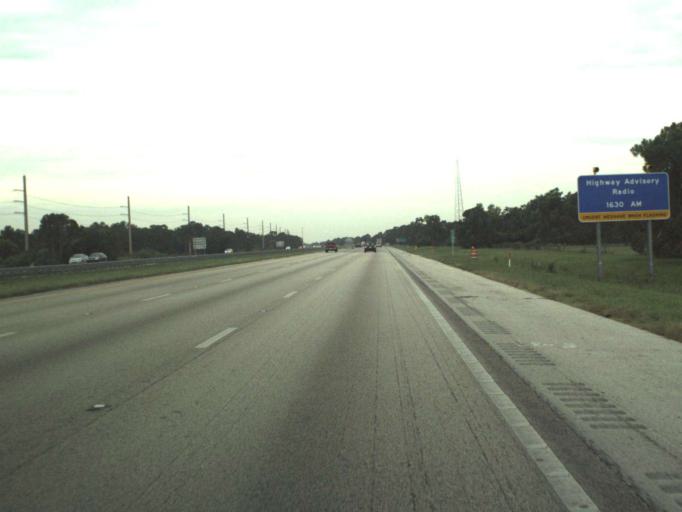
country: US
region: Florida
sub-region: Martin County
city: Palm City
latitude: 27.0992
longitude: -80.2573
